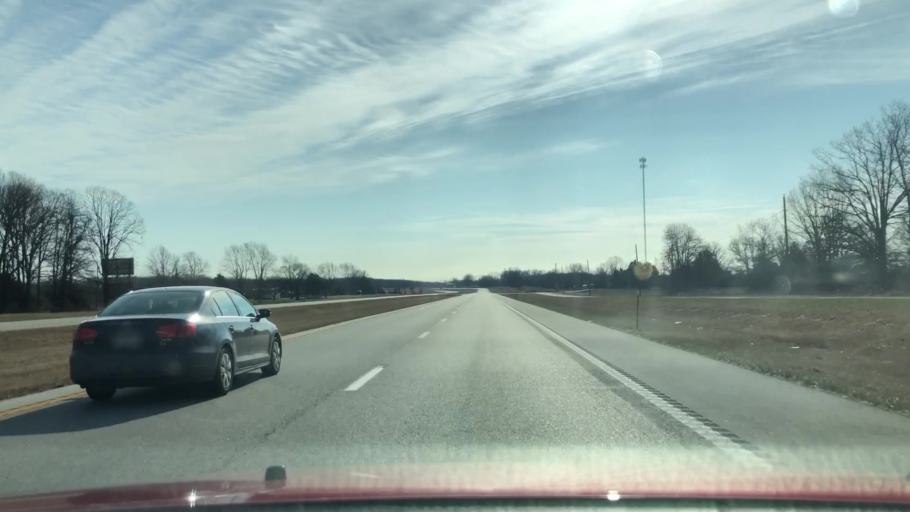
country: US
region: Missouri
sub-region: Webster County
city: Seymour
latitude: 37.1412
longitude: -92.7463
